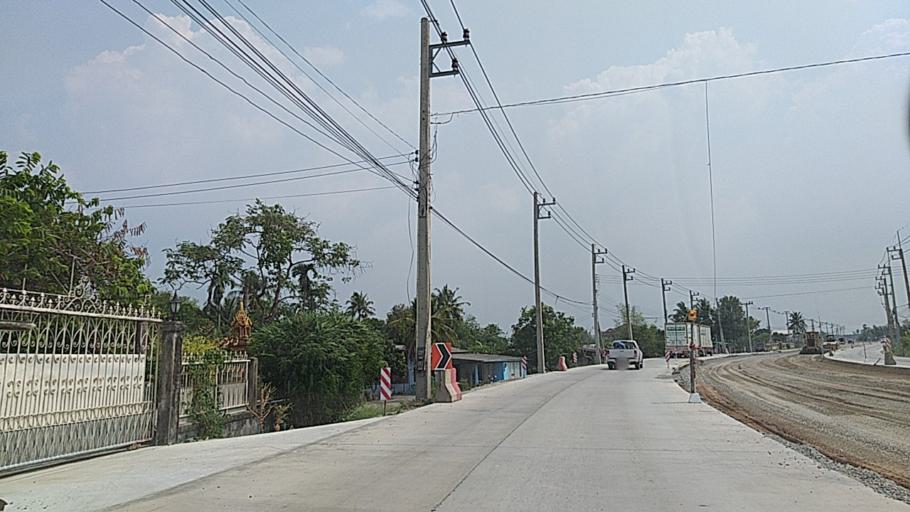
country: TH
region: Chon Buri
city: Phanat Nikhom
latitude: 13.3942
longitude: 101.1923
